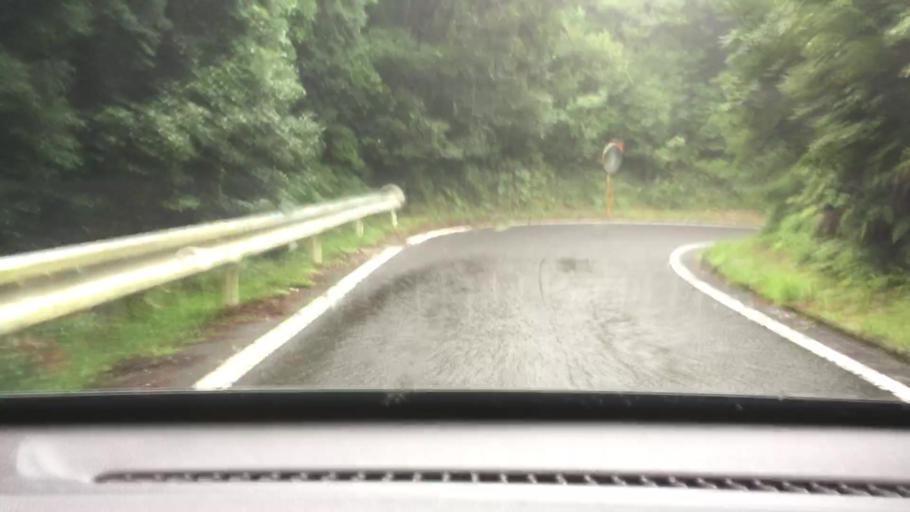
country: JP
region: Nagasaki
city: Togitsu
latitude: 32.9161
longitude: 129.7305
